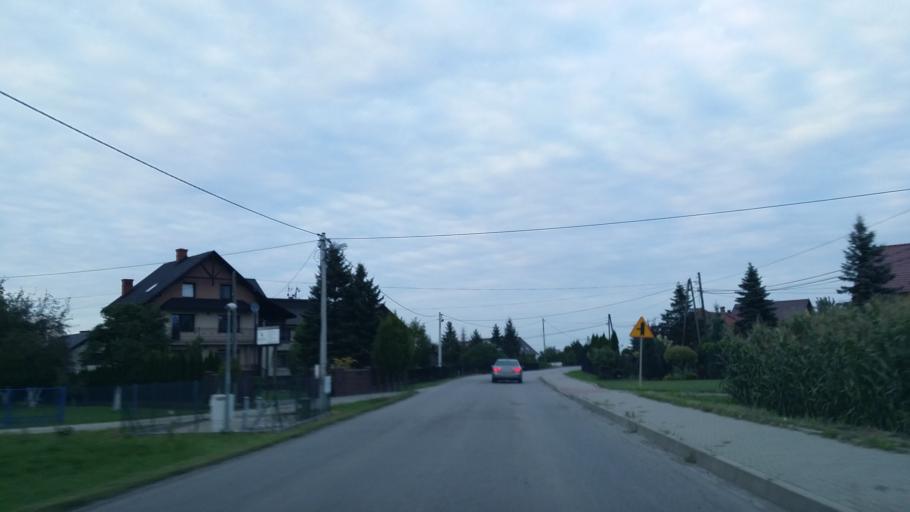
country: PL
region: Lesser Poland Voivodeship
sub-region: Powiat krakowski
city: Kaszow
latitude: 50.0194
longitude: 19.7238
